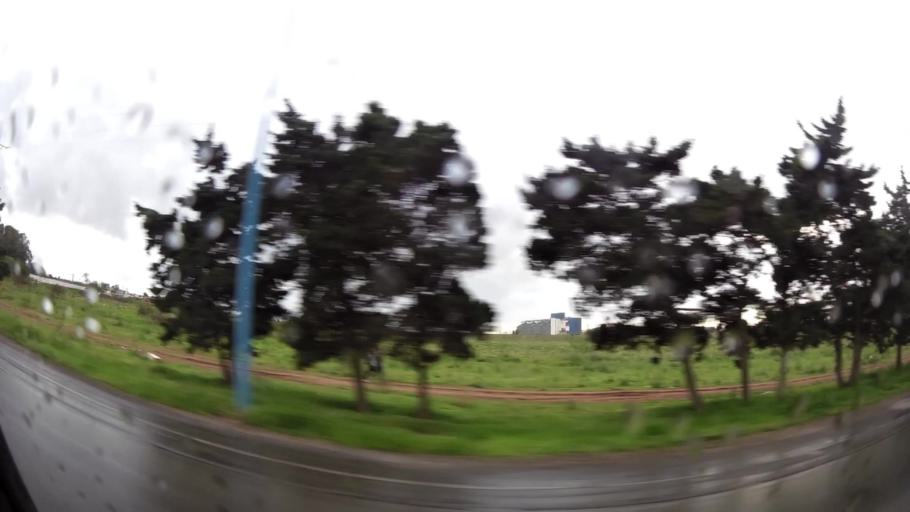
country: MA
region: Grand Casablanca
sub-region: Mohammedia
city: Mohammedia
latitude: 33.6726
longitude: -7.4070
